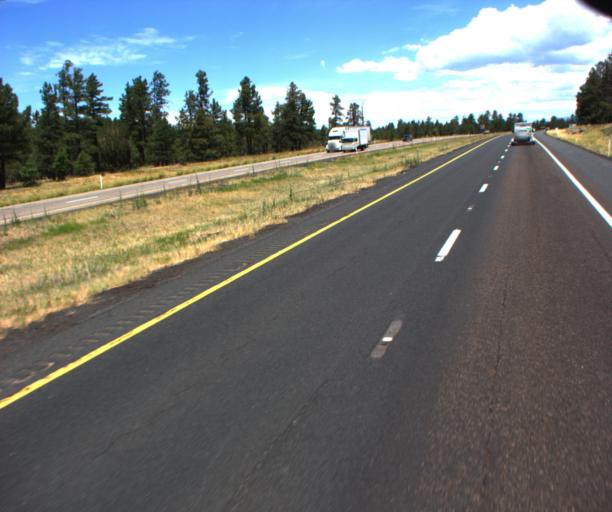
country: US
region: Arizona
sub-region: Coconino County
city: Sedona
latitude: 34.9001
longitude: -111.6415
